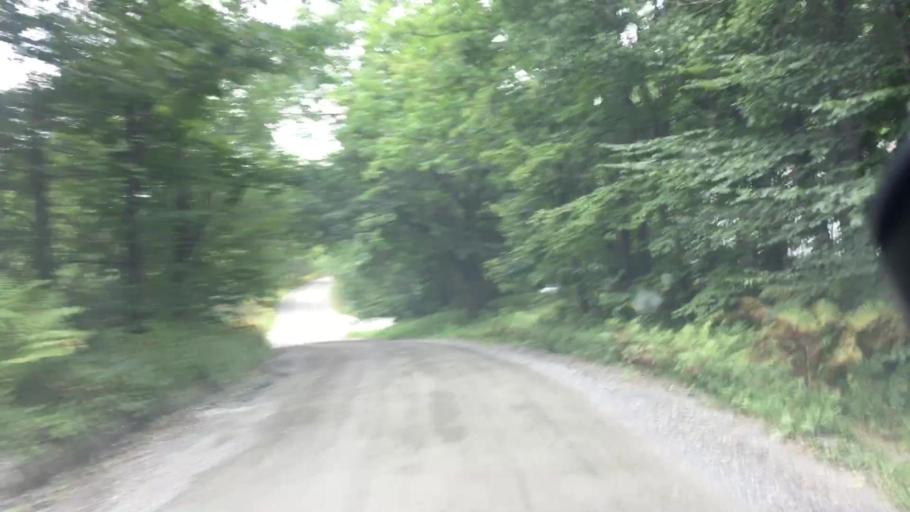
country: US
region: Vermont
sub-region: Windham County
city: Dover
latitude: 42.8608
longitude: -72.7812
